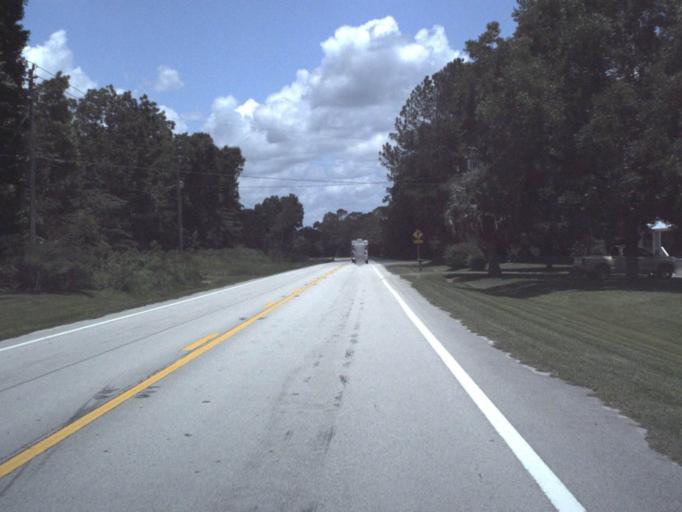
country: US
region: Florida
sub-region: Bradford County
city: Starke
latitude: 30.0132
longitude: -82.1443
